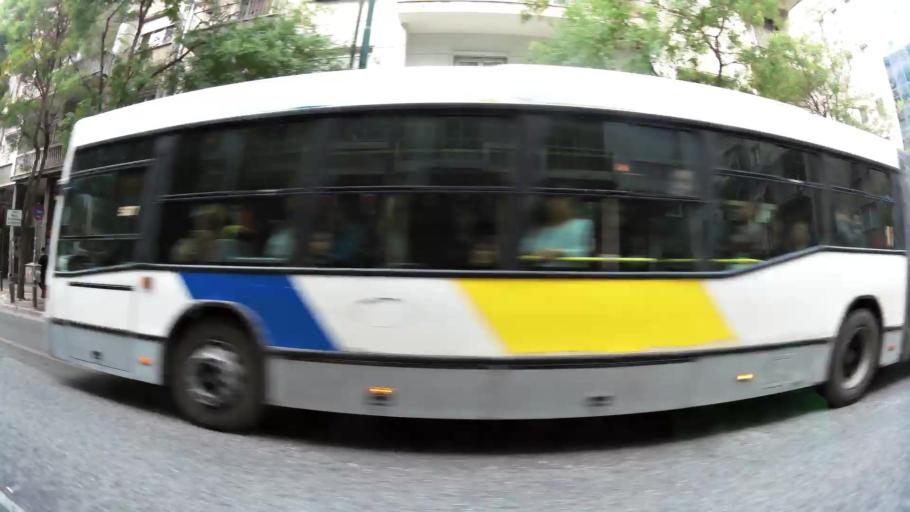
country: GR
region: Attica
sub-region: Nomarchia Athinas
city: Kipseli
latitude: 38.0008
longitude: 23.7334
